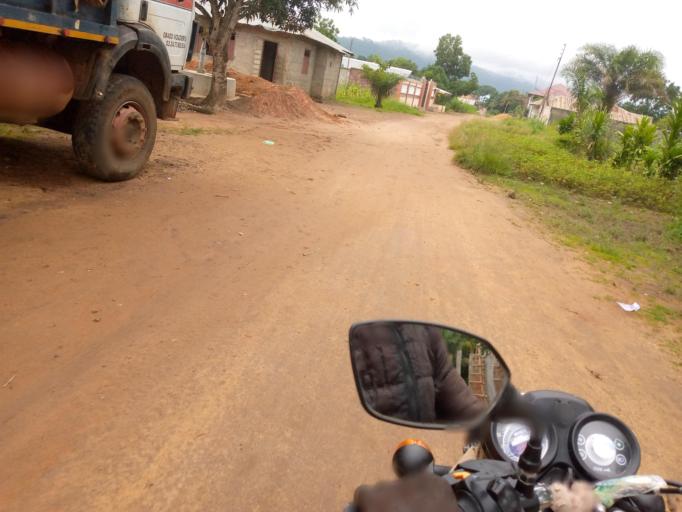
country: SL
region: Eastern Province
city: Kenema
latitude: 7.8423
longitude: -11.2024
